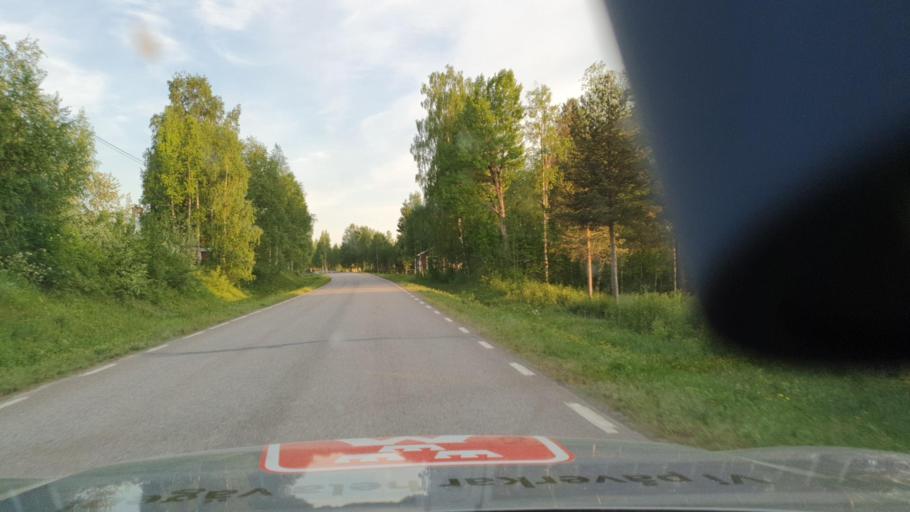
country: SE
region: Norrbotten
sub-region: Bodens Kommun
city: Boden
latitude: 66.0377
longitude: 21.8037
